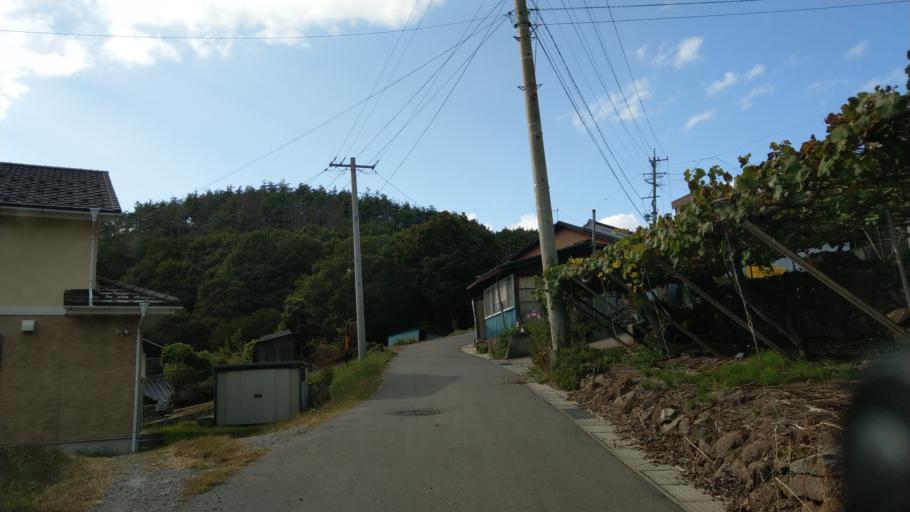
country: JP
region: Nagano
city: Komoro
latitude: 36.3427
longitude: 138.4162
